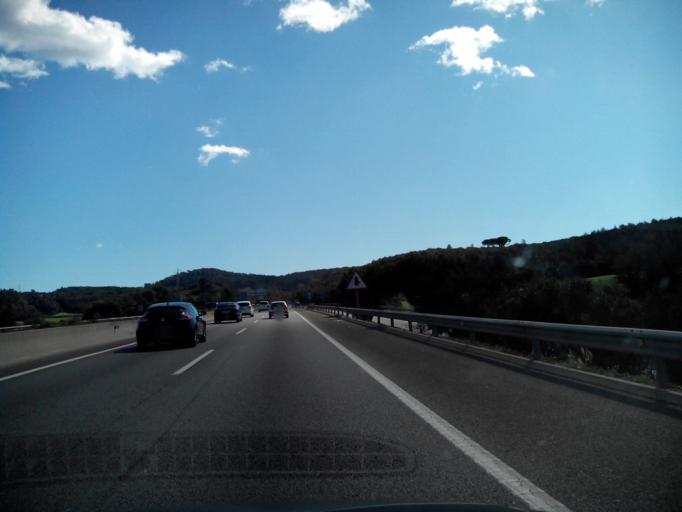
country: ES
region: Catalonia
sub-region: Provincia de Barcelona
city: La Roca del Valles
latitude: 41.5926
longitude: 2.3424
